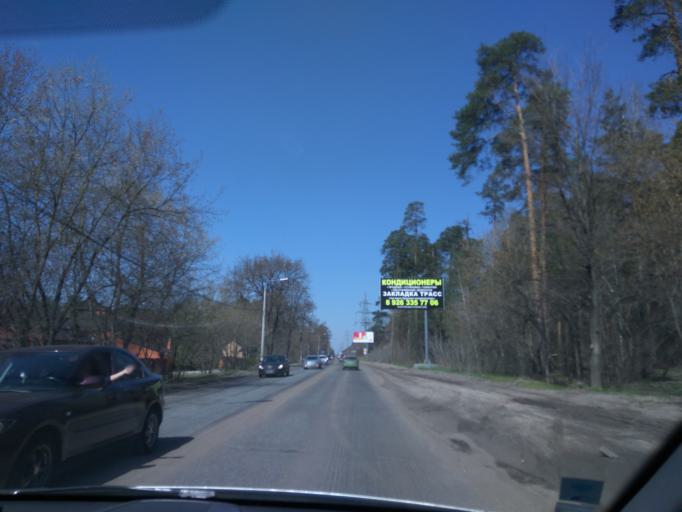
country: RU
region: Moskovskaya
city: Kratovo
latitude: 55.5680
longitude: 38.1951
